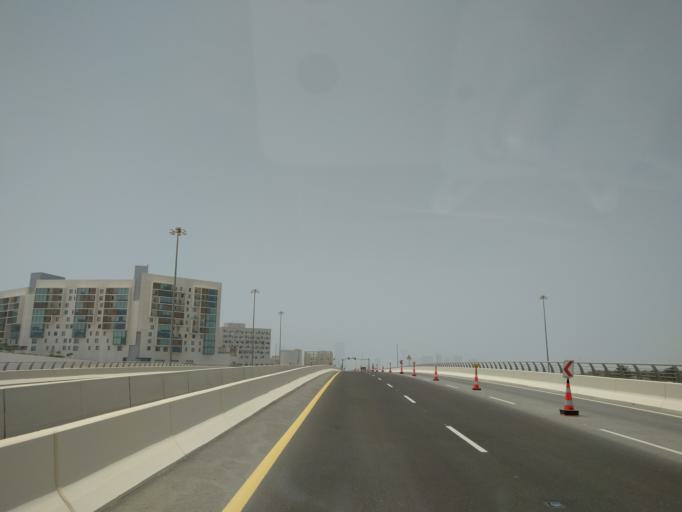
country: AE
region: Abu Dhabi
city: Abu Dhabi
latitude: 24.5279
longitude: 54.4345
